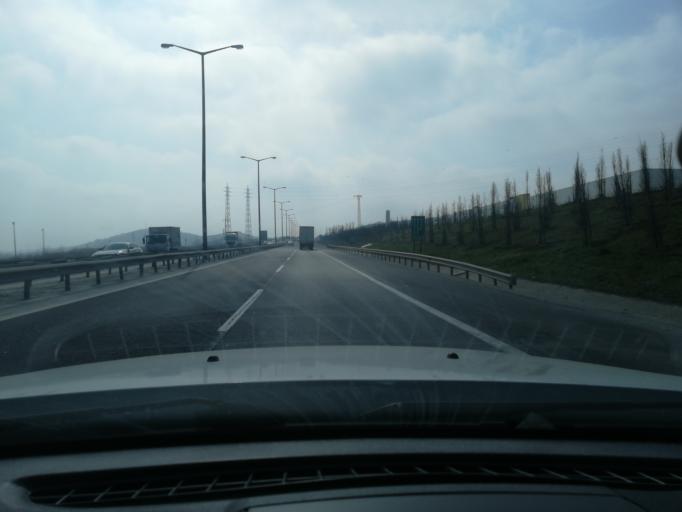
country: TR
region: Istanbul
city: Muratbey
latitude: 41.0796
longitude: 28.5078
